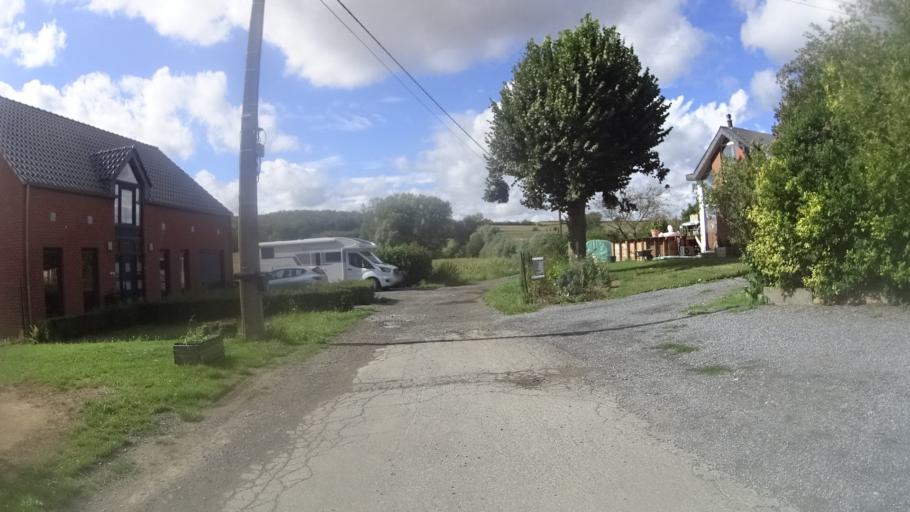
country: BE
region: Wallonia
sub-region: Province du Hainaut
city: Merbes-le-Chateau
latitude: 50.3218
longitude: 4.2113
